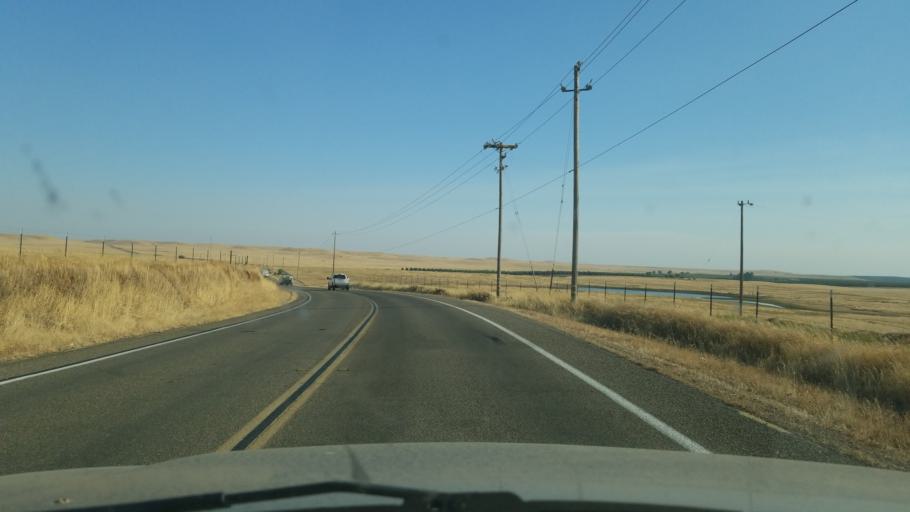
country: US
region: California
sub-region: Merced County
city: Merced
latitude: 37.4880
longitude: -120.4466
